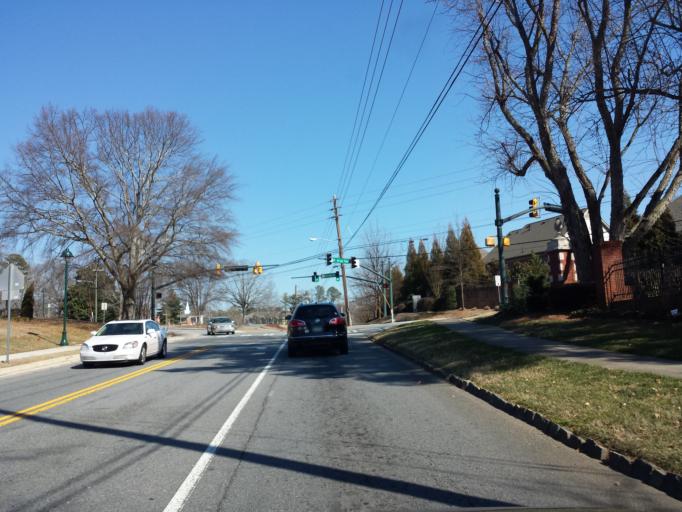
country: US
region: Georgia
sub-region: Fulton County
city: Sandy Springs
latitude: 33.9266
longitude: -84.3672
